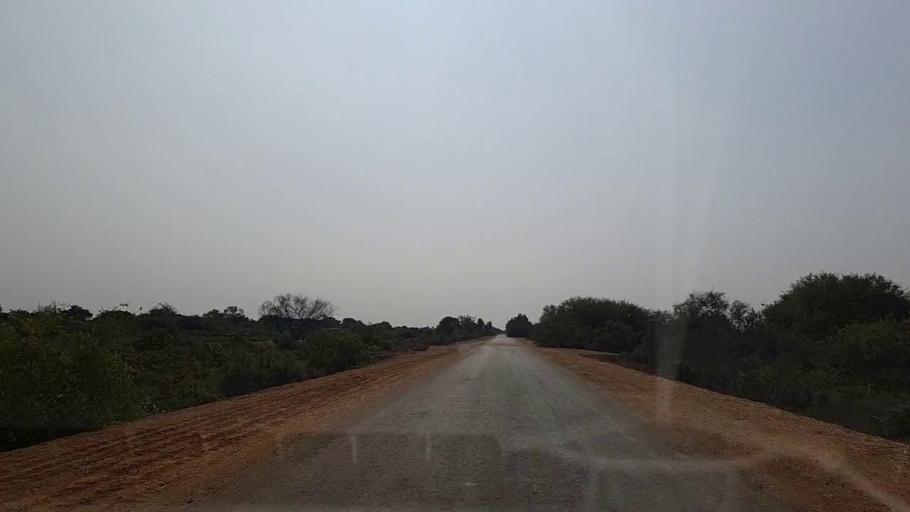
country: PK
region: Sindh
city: Chuhar Jamali
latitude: 24.2603
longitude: 67.9080
